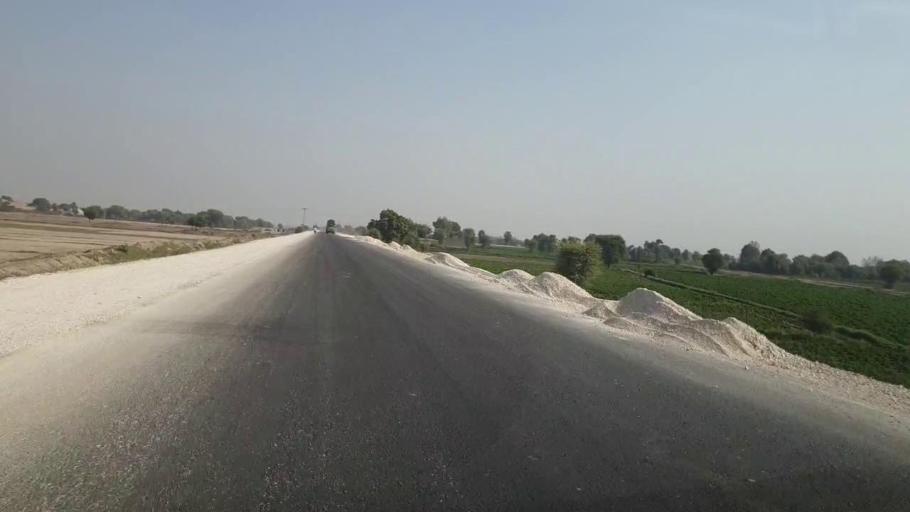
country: PK
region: Sindh
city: Bhan
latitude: 26.5507
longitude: 67.7823
